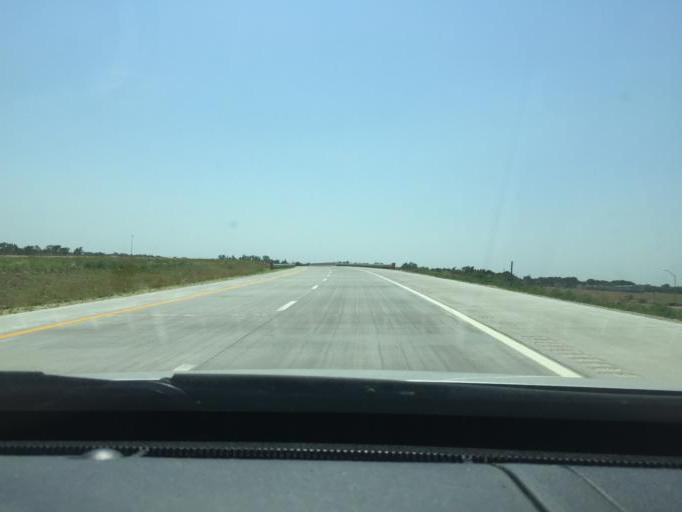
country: US
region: Kansas
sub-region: Reno County
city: South Hutchinson
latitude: 38.0287
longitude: -97.9011
